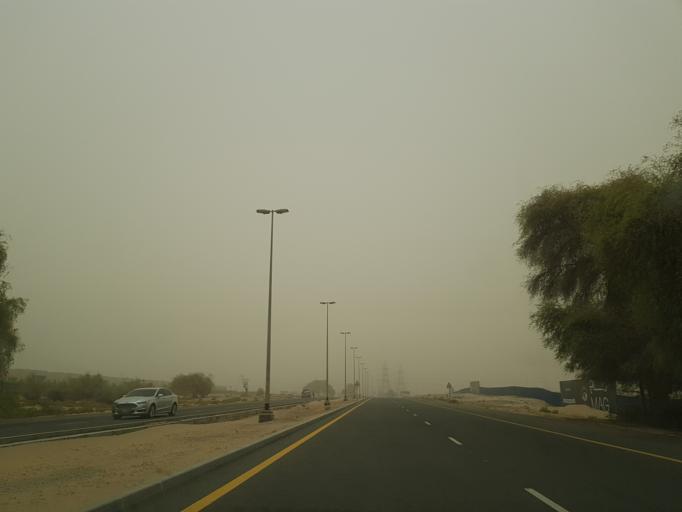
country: AE
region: Dubai
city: Dubai
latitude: 25.1441
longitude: 55.2879
